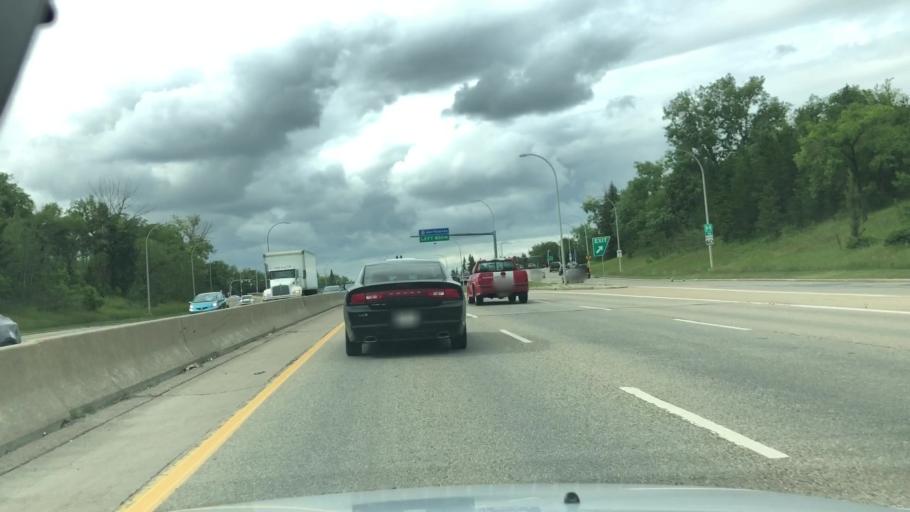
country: CA
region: Alberta
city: Edmonton
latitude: 53.5608
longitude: -113.4436
